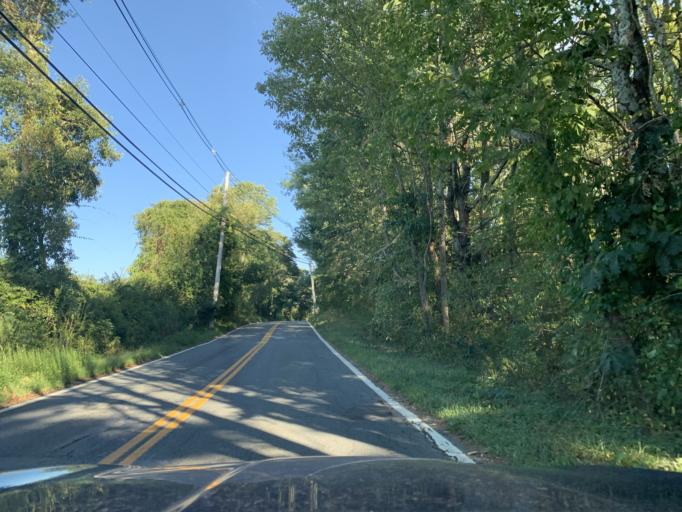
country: US
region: Rhode Island
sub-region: Washington County
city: Exeter
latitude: 41.5448
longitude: -71.5214
